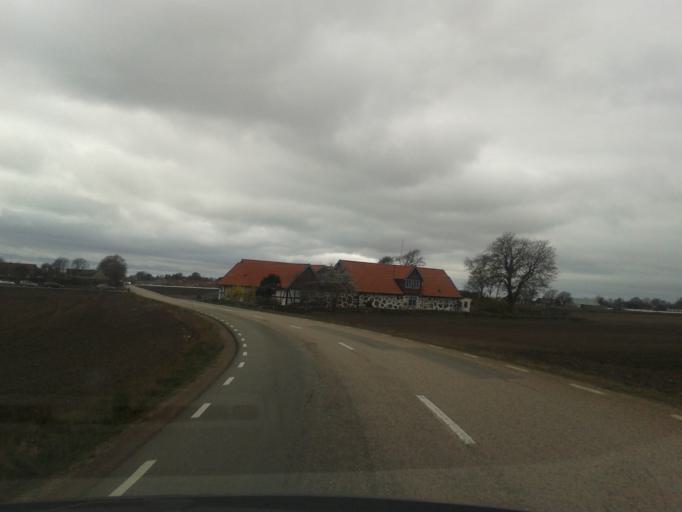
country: SE
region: Skane
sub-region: Angelholms Kommun
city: Vejbystrand
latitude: 56.3176
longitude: 12.7824
